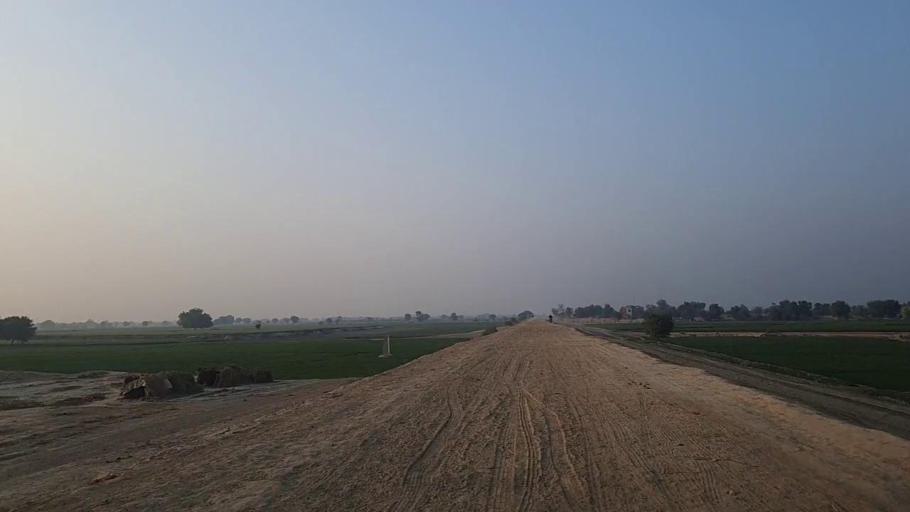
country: PK
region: Sindh
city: Sann
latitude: 26.1897
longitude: 68.0913
